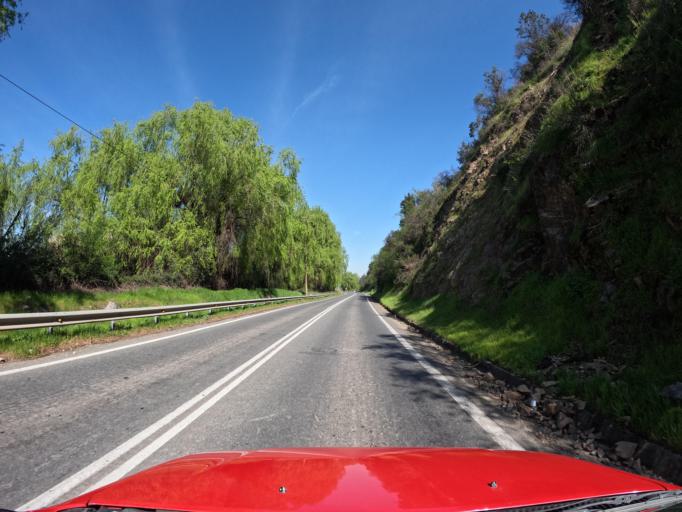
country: CL
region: Maule
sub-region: Provincia de Curico
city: Rauco
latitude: -34.9888
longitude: -71.4289
